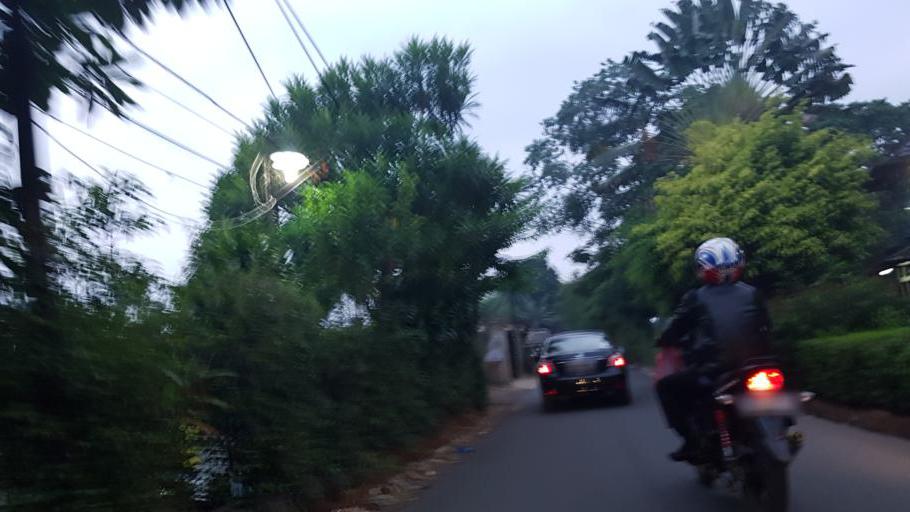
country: ID
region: West Java
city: Depok
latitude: -6.3637
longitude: 106.8000
